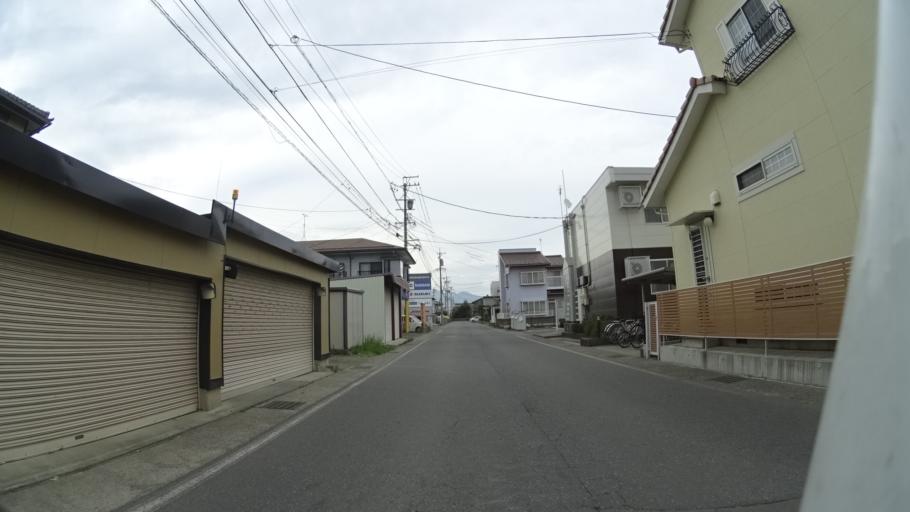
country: JP
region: Nagano
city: Nagano-shi
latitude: 36.5670
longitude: 138.1424
